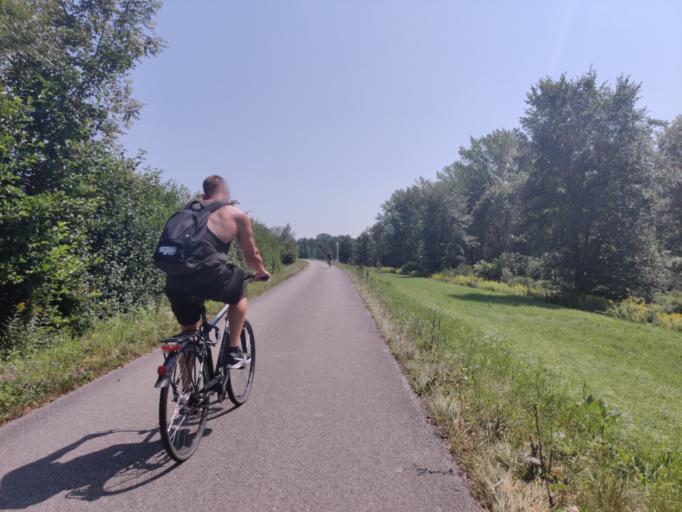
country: AT
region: Upper Austria
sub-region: Politischer Bezirk Urfahr-Umgebung
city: Goldworth
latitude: 48.3089
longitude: 14.1078
